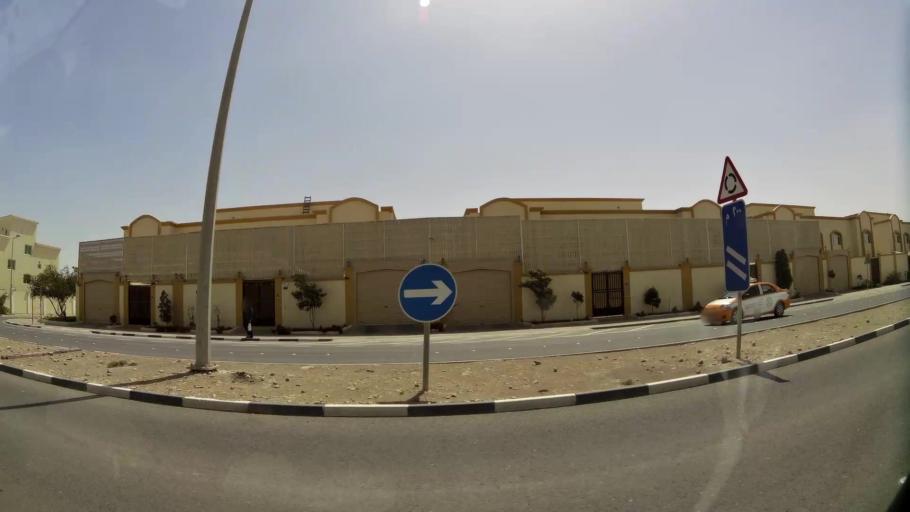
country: QA
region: Baladiyat Umm Salal
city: Umm Salal Muhammad
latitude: 25.3650
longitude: 51.4334
